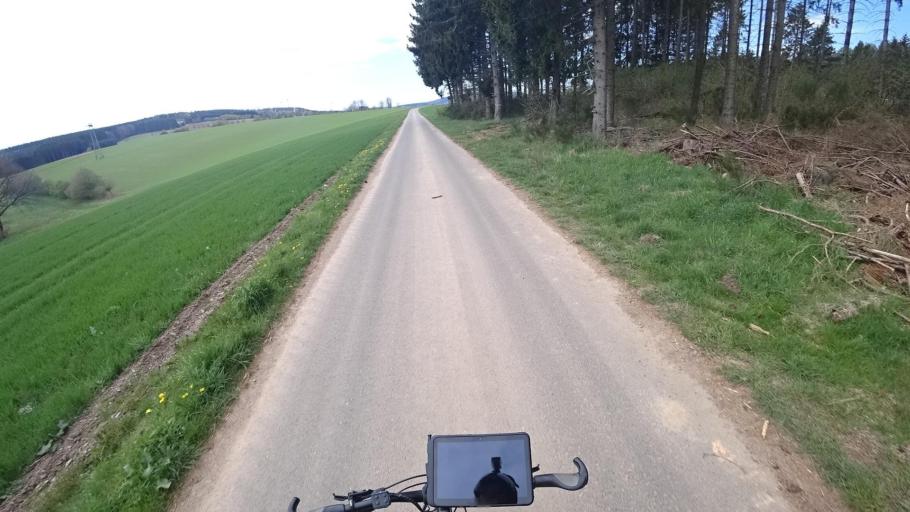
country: DE
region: Rheinland-Pfalz
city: Gusenburg
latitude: 49.6408
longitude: 6.9188
